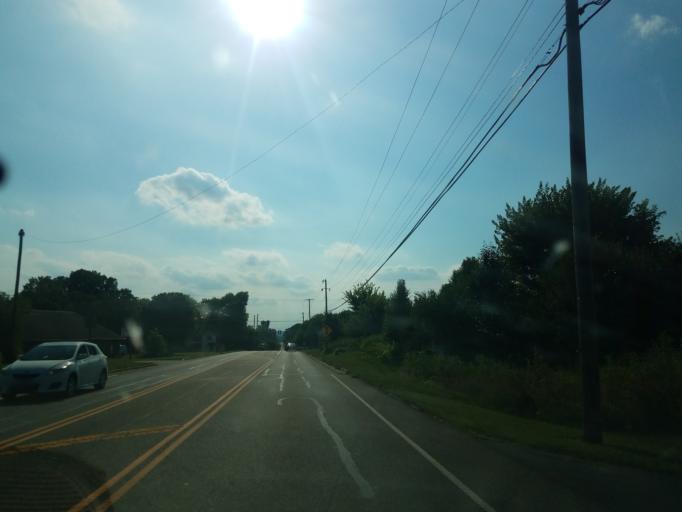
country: US
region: Ohio
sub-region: Summit County
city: New Franklin
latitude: 40.8808
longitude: -81.5308
